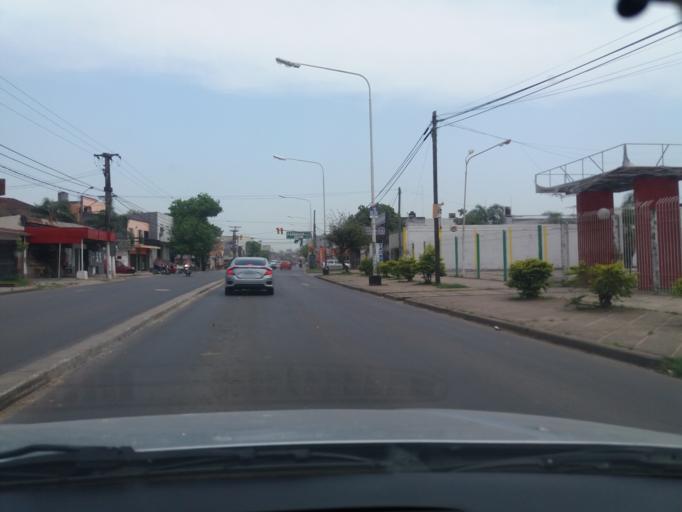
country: AR
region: Corrientes
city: Corrientes
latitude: -27.4920
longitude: -58.8193
